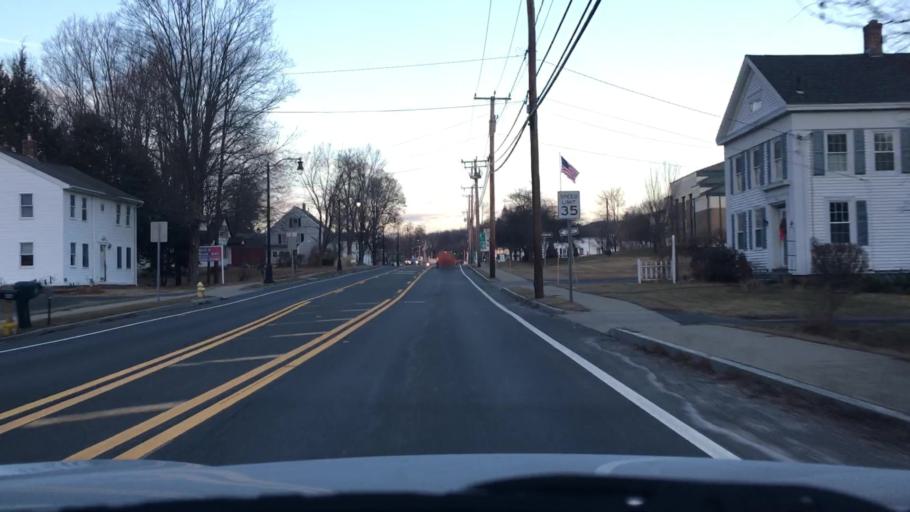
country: US
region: Massachusetts
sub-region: Hampden County
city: Southwick
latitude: 42.0527
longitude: -72.7726
